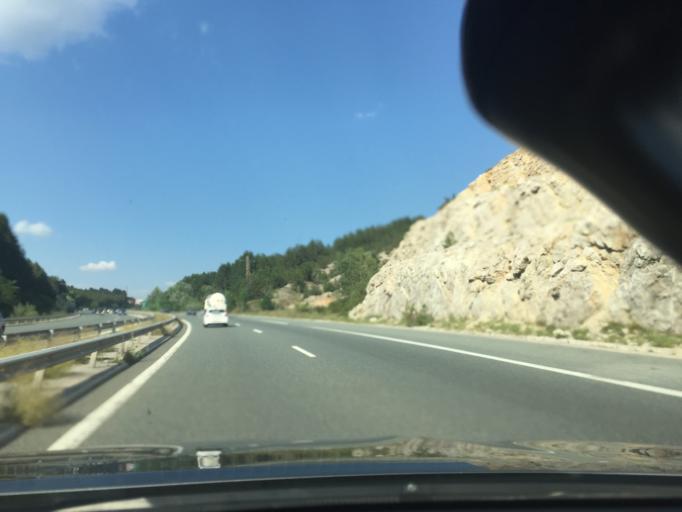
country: BG
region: Pernik
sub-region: Obshtina Pernik
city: Pernik
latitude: 42.4915
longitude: 23.1323
